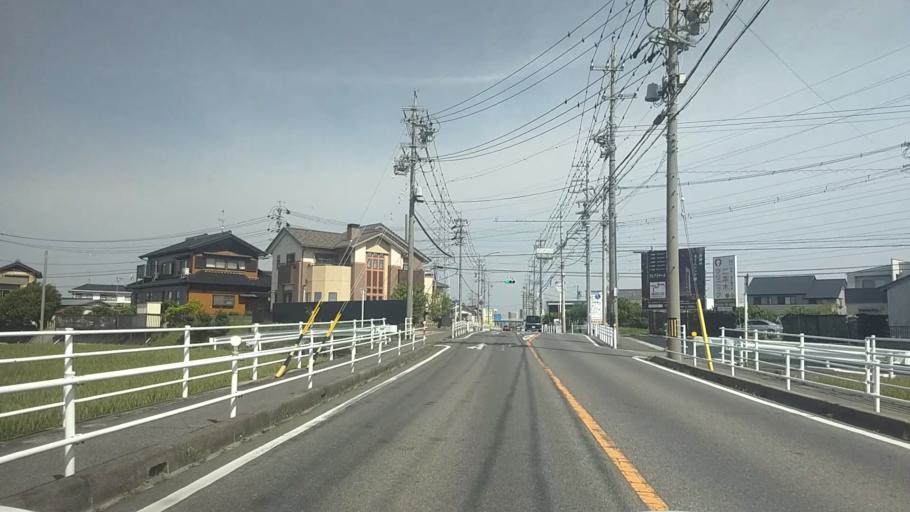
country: JP
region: Aichi
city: Anjo
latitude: 34.9569
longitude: 137.0657
